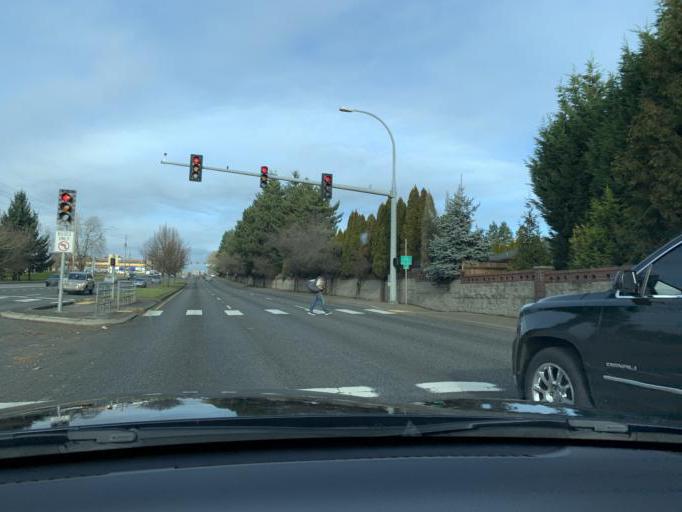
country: US
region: Washington
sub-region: Clark County
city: Mill Plain
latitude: 45.5941
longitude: -122.5038
